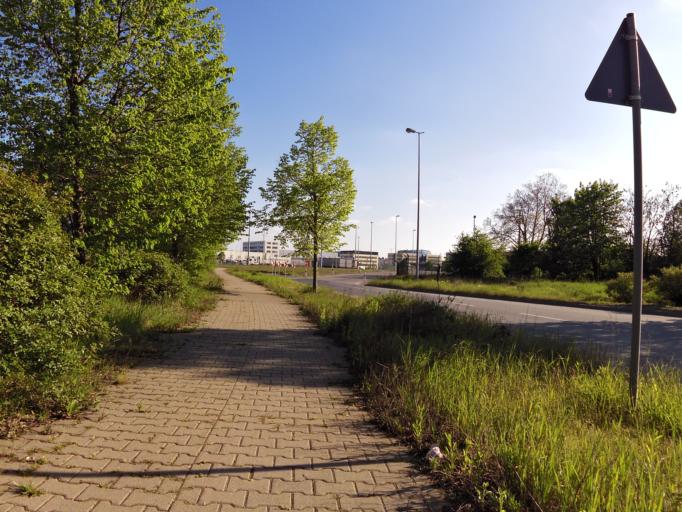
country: DE
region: Hesse
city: Morfelden-Walldorf
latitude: 50.0290
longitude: 8.5888
